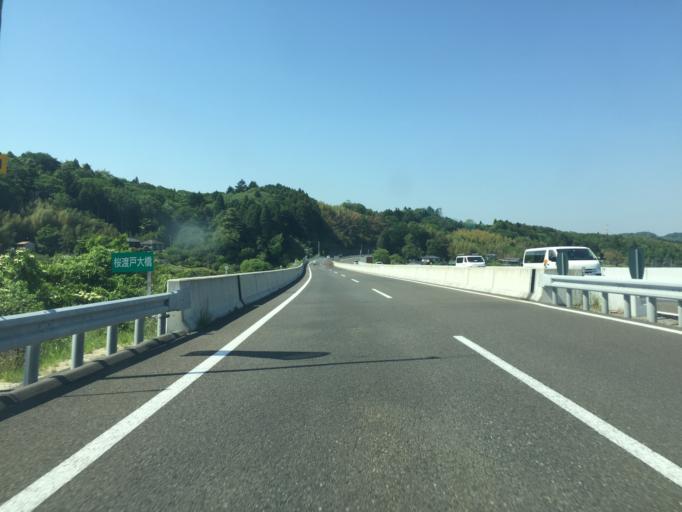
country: JP
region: Miyagi
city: Matsushima
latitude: 38.3825
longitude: 141.0344
